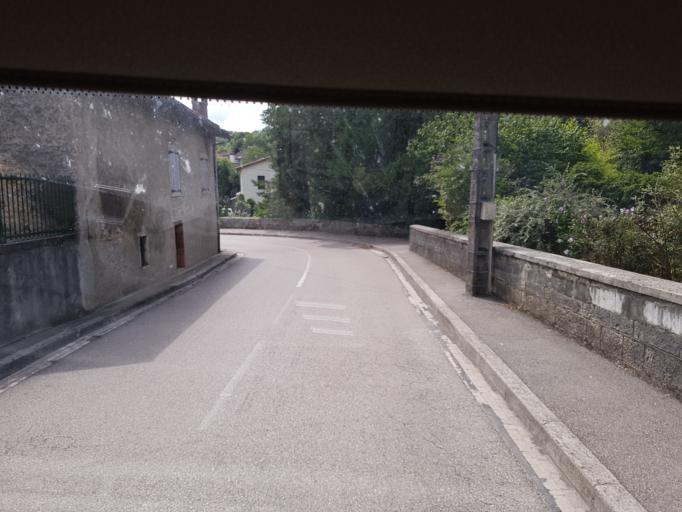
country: FR
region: Rhone-Alpes
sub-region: Departement de l'Ain
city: Poncin
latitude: 46.0852
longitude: 5.4063
